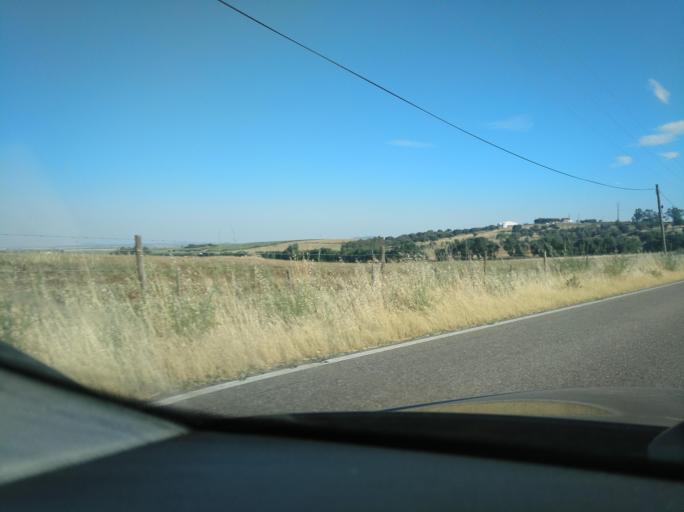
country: PT
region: Portalegre
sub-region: Elvas
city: Elvas
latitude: 38.8294
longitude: -7.1658
